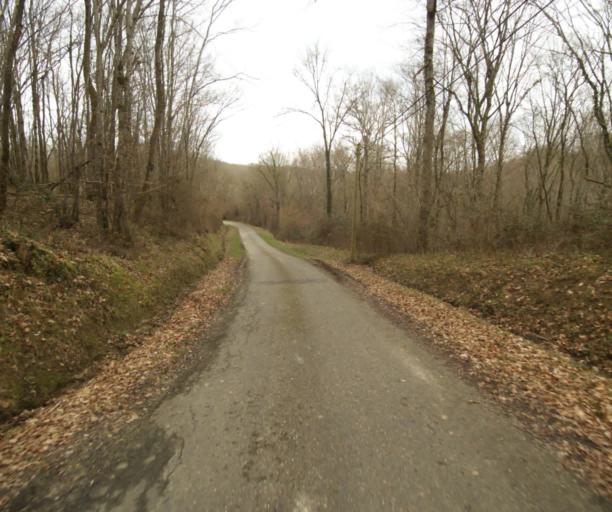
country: FR
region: Aquitaine
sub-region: Departement des Landes
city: Gabarret
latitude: 43.9291
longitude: 0.0352
